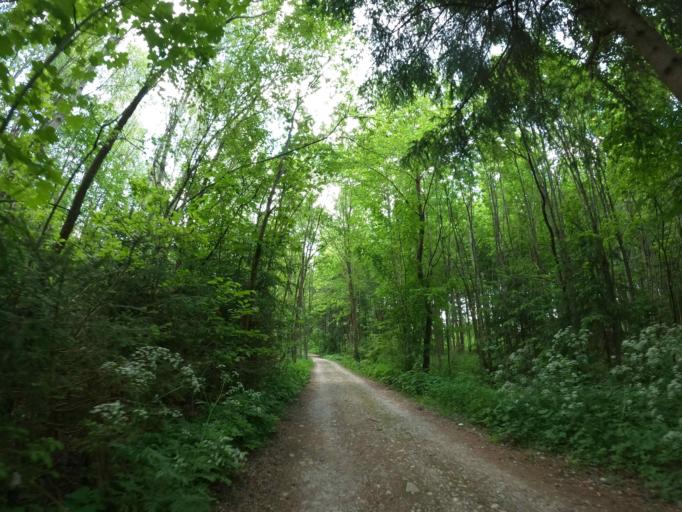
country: DE
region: Bavaria
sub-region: Upper Bavaria
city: Sauerlach
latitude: 47.9865
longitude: 11.6422
